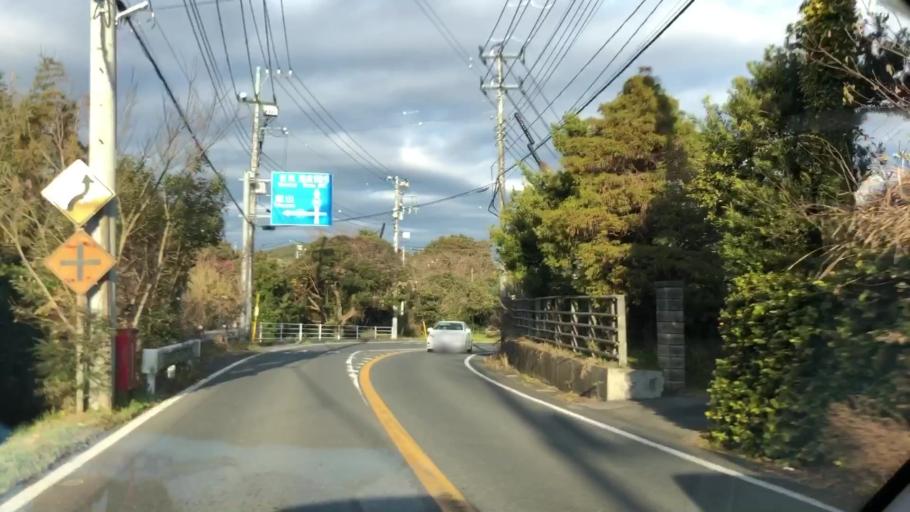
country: JP
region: Chiba
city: Tateyama
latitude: 34.9825
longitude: 139.9458
